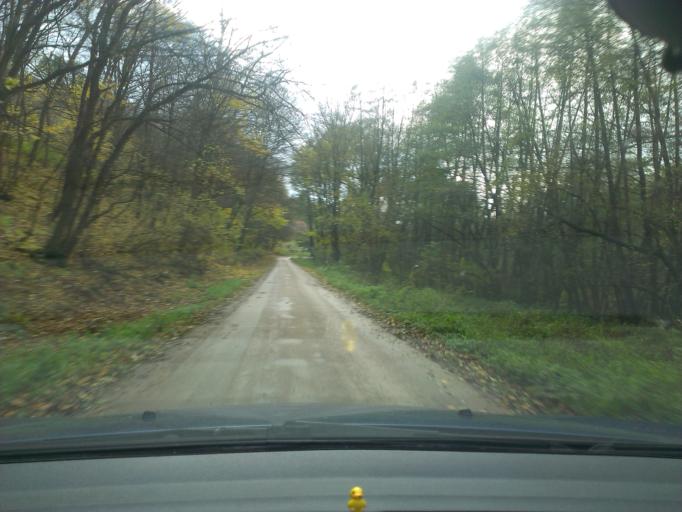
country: SK
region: Trnavsky
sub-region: Okres Trnava
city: Piestany
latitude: 48.6068
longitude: 17.8923
